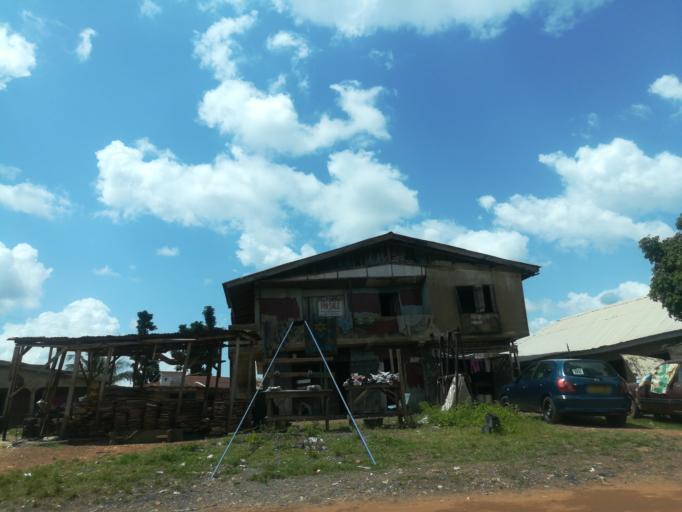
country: NG
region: Oyo
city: Lalupon
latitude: 7.4379
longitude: 4.0055
